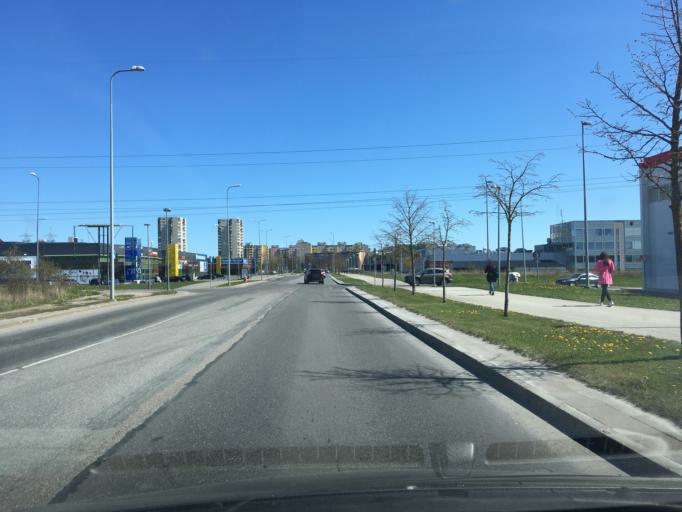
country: EE
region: Harju
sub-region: Tallinna linn
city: Kose
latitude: 59.4429
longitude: 24.8574
